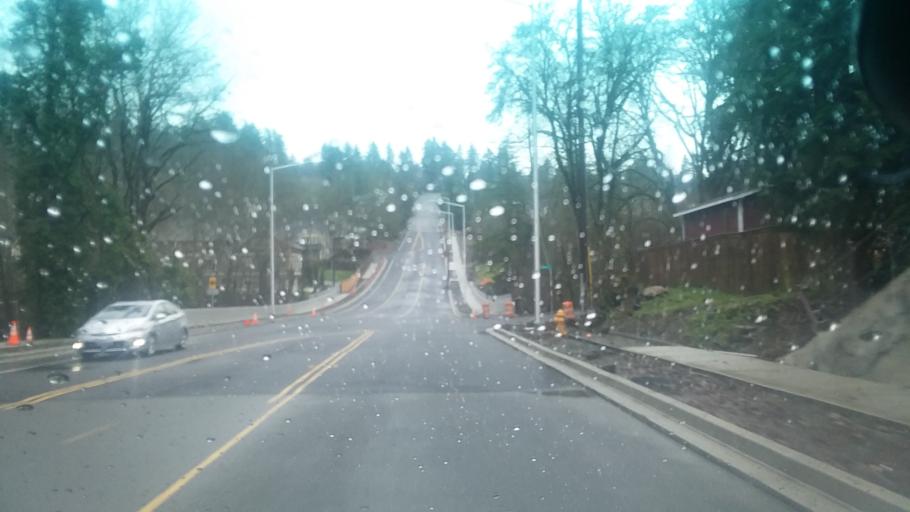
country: US
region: Washington
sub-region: King County
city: Kent
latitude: 47.4067
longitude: -122.2172
